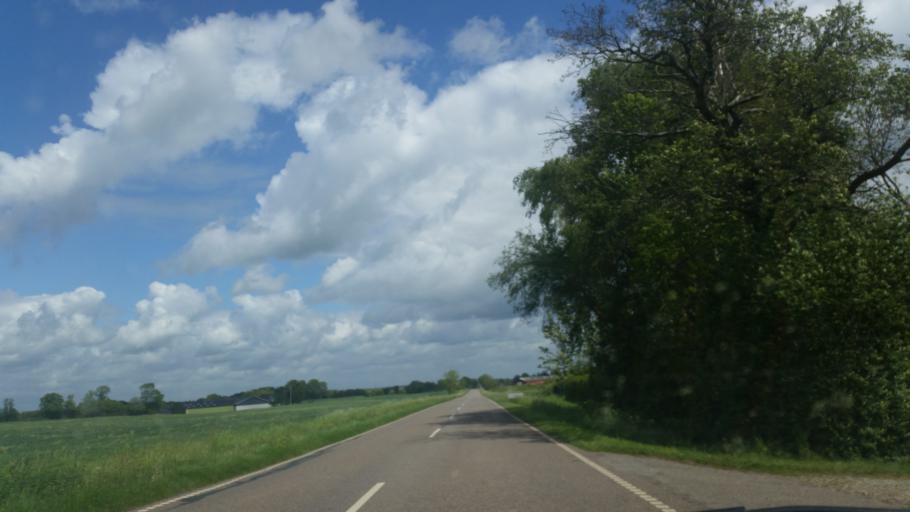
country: DK
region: South Denmark
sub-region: Kolding Kommune
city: Christiansfeld
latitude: 55.3346
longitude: 9.4526
